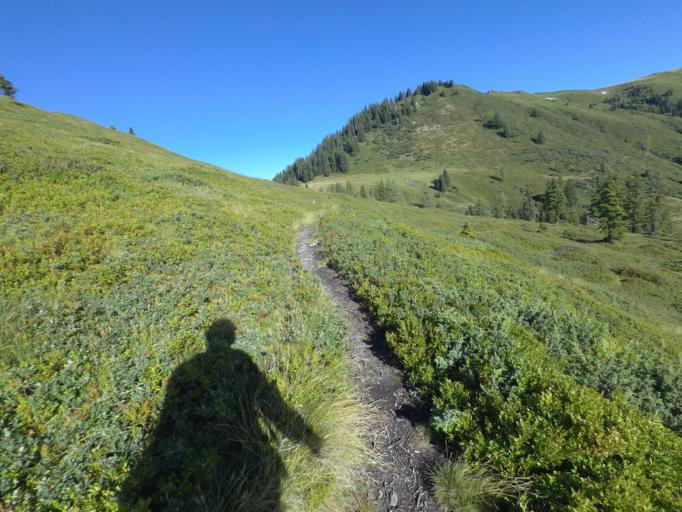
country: AT
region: Salzburg
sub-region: Politischer Bezirk Sankt Johann im Pongau
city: Goldegg
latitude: 47.3578
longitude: 13.0751
